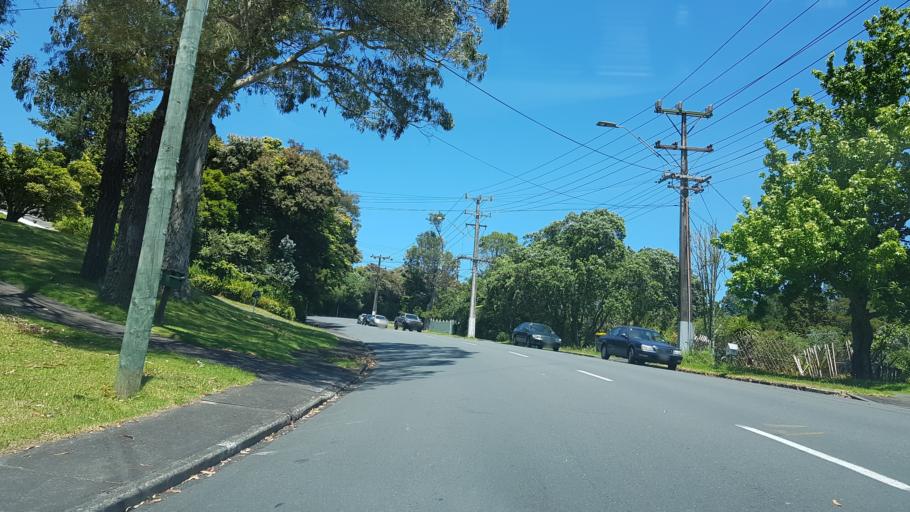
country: NZ
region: Auckland
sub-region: Auckland
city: North Shore
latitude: -36.7902
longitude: 174.7274
